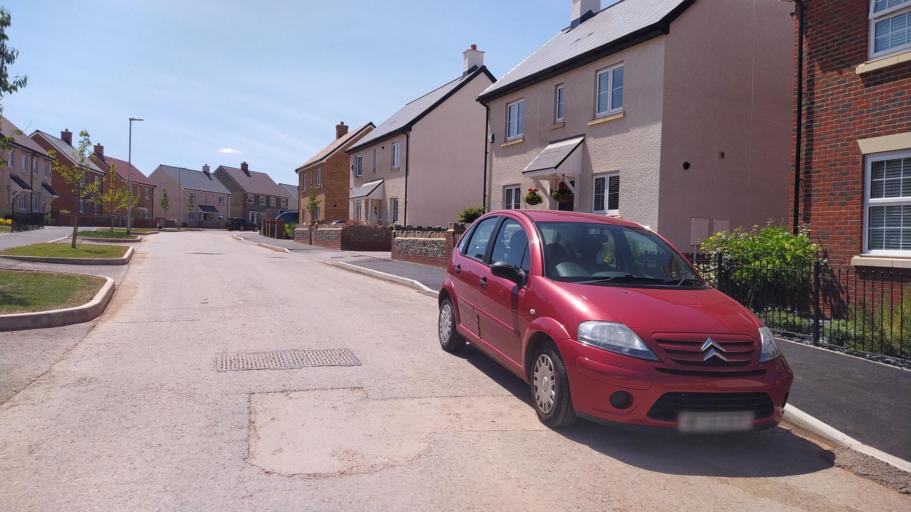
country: GB
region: England
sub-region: Somerset
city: Taunton
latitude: 51.0022
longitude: -3.0922
